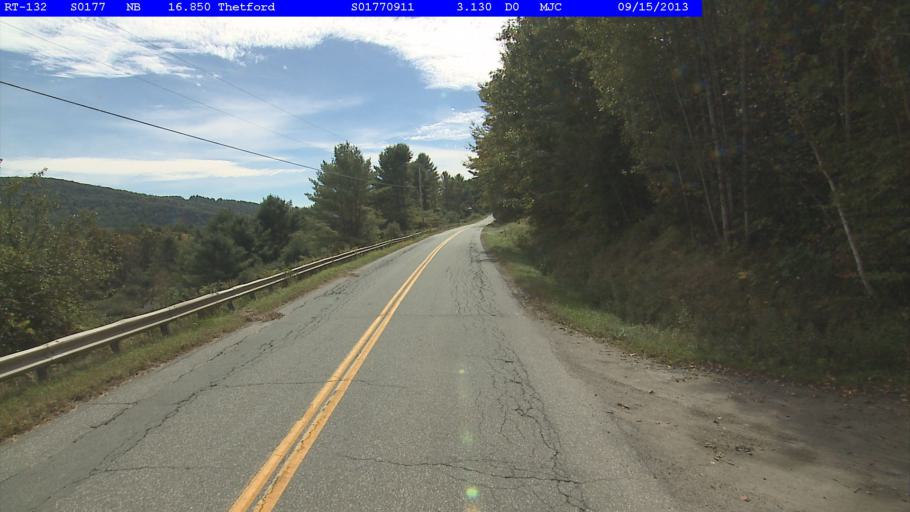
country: US
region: New Hampshire
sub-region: Grafton County
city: Hanover
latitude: 43.8132
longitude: -72.2747
